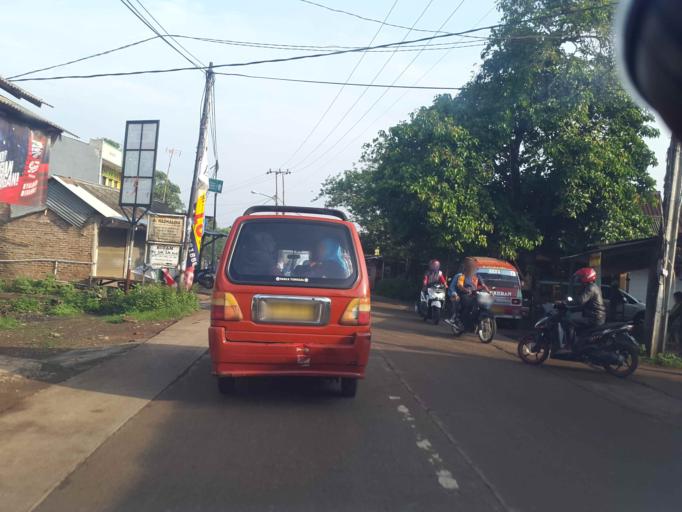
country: ID
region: West Java
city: Bekasi
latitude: -6.3242
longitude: 107.0392
